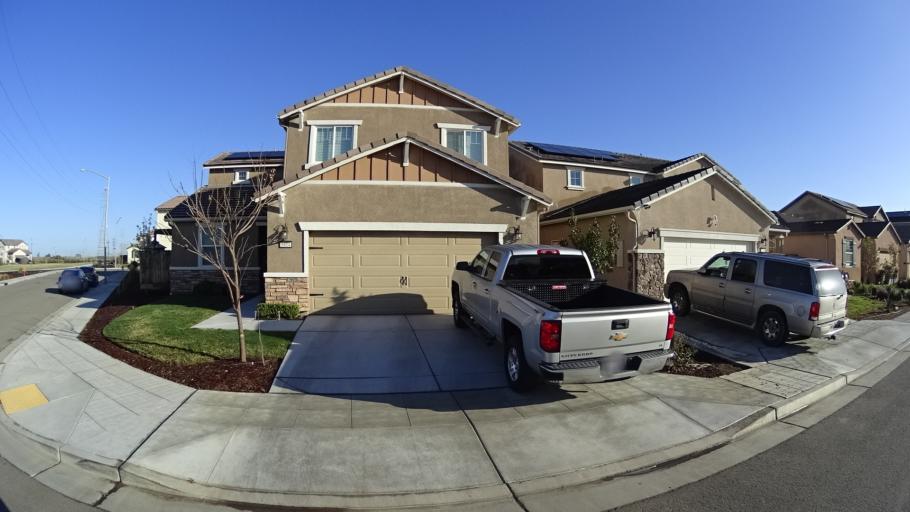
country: US
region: California
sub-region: Fresno County
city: Biola
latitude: 36.8381
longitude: -119.9134
